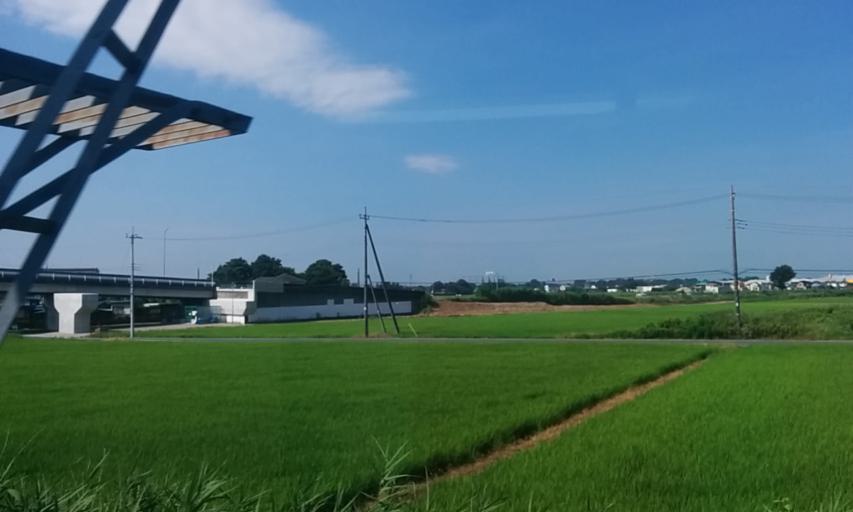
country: JP
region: Saitama
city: Hanyu
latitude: 36.1445
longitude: 139.5643
